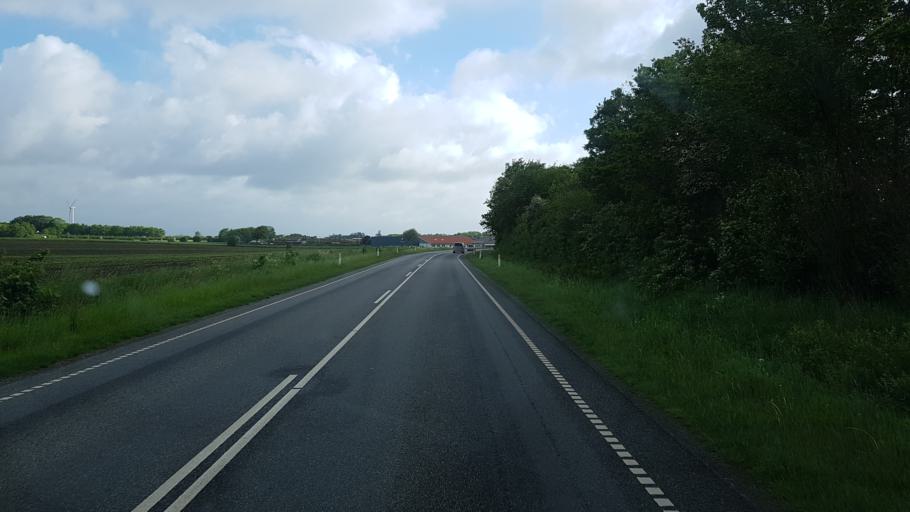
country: DK
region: South Denmark
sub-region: Vejen Kommune
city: Vejen
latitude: 55.4181
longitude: 9.1387
